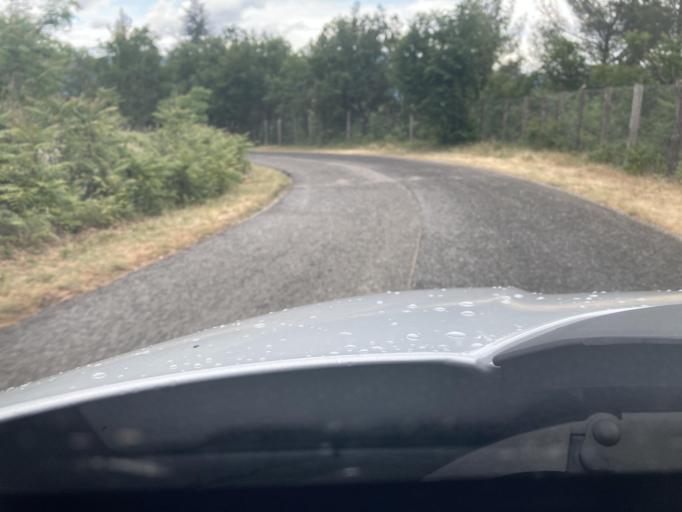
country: IT
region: Abruzzo
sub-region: Provincia dell' Aquila
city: Fossa
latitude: 42.2827
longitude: 13.4938
